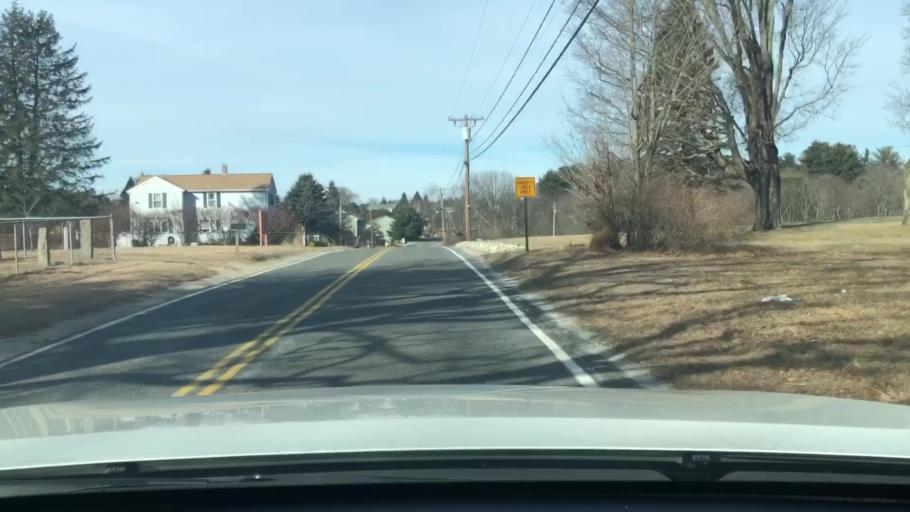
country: US
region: Massachusetts
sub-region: Worcester County
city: Blackstone
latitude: 42.0526
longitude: -71.5219
